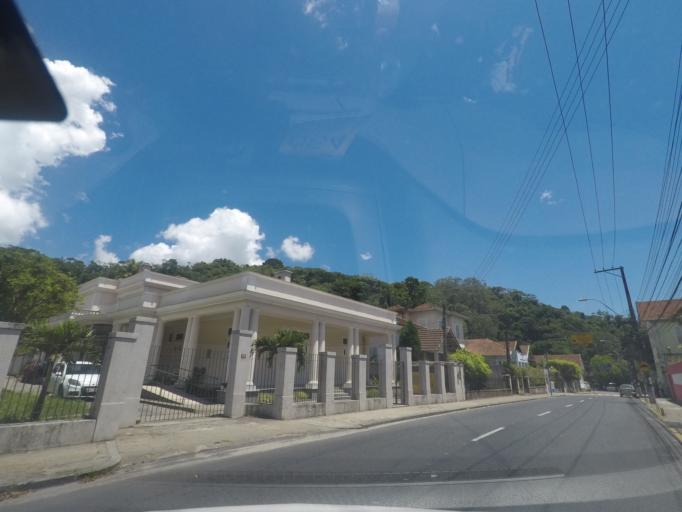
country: BR
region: Rio de Janeiro
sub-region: Petropolis
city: Petropolis
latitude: -22.5138
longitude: -43.1727
